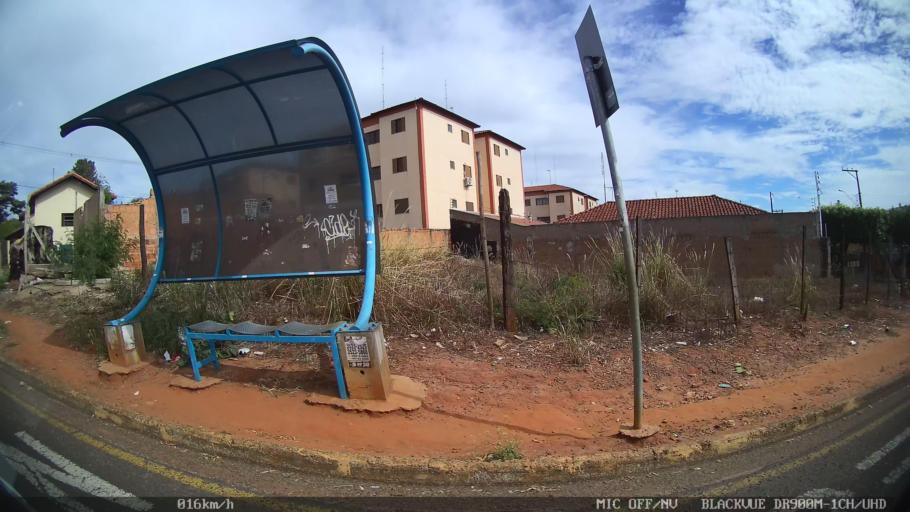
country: BR
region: Sao Paulo
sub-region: Catanduva
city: Catanduva
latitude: -21.1533
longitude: -48.9635
